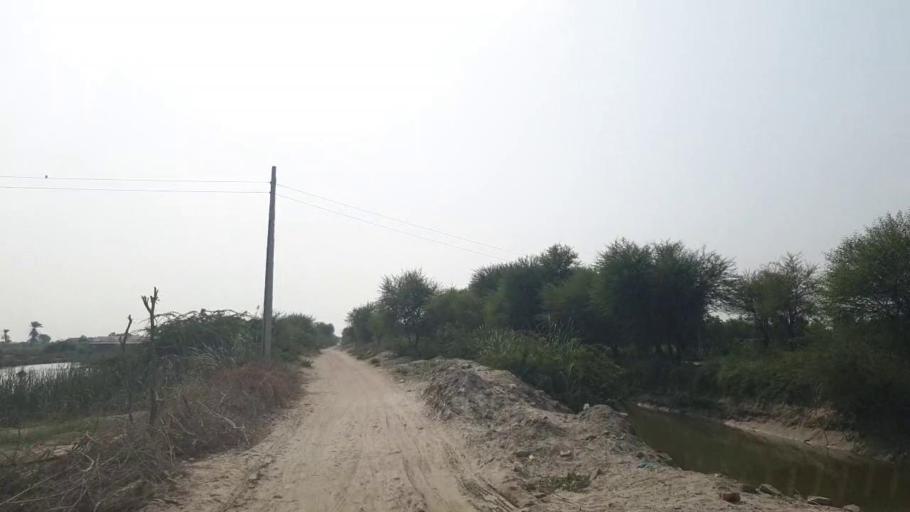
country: PK
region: Sindh
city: Badin
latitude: 24.6129
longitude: 68.7219
